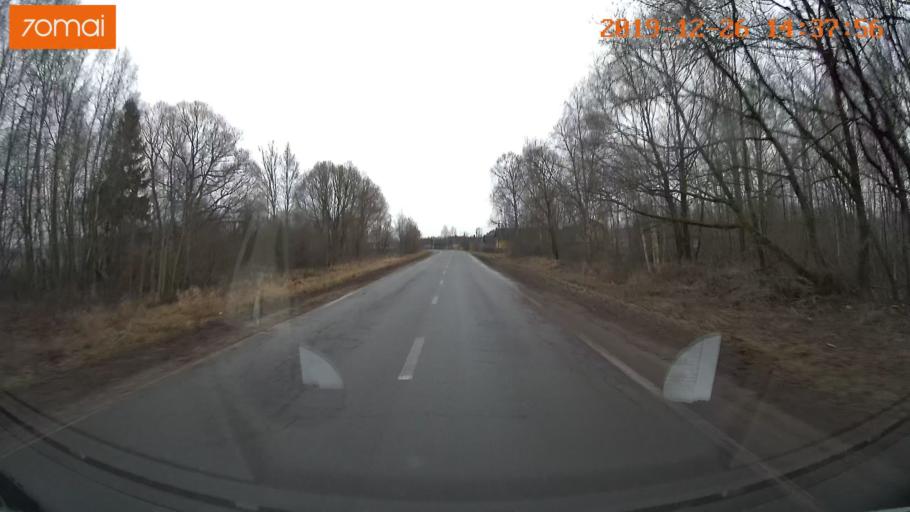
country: RU
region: Jaroslavl
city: Poshekhon'ye
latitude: 58.3983
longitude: 38.9716
